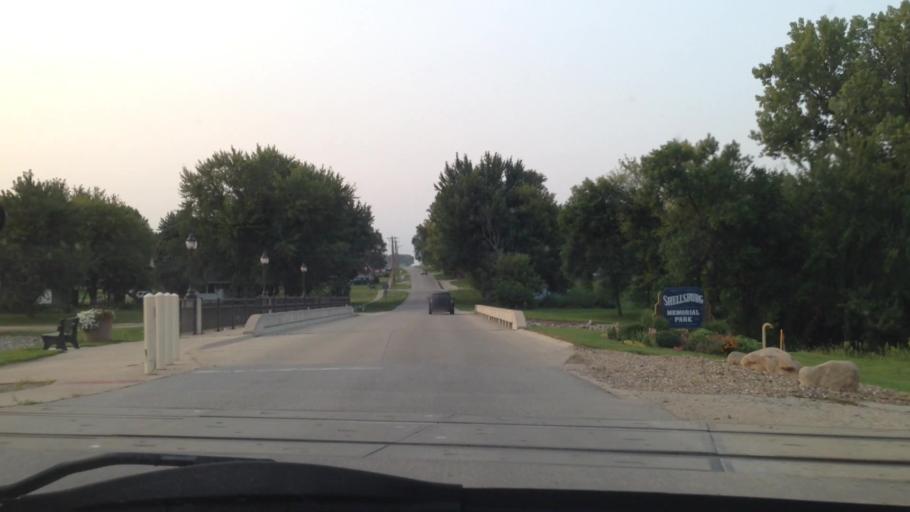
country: US
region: Iowa
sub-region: Linn County
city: Palo
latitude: 42.0927
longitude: -91.8734
